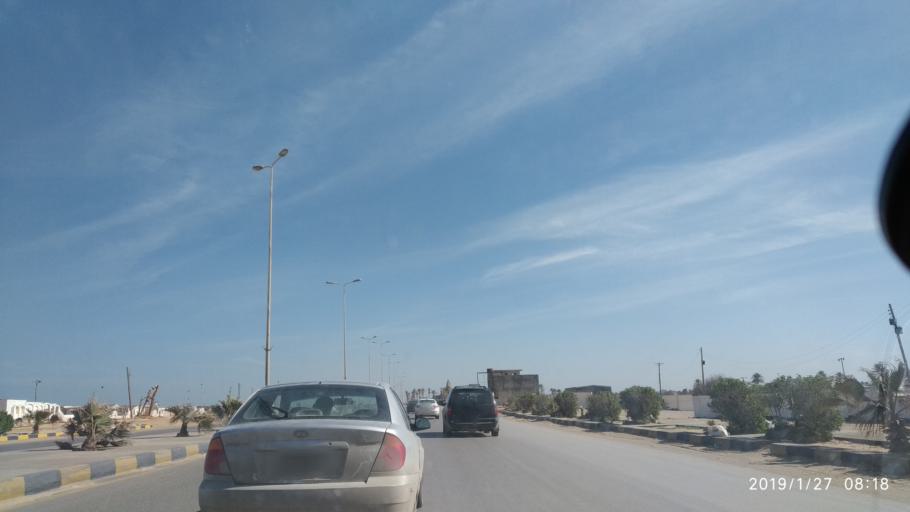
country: LY
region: Tripoli
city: Tagiura
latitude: 32.8954
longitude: 13.3284
